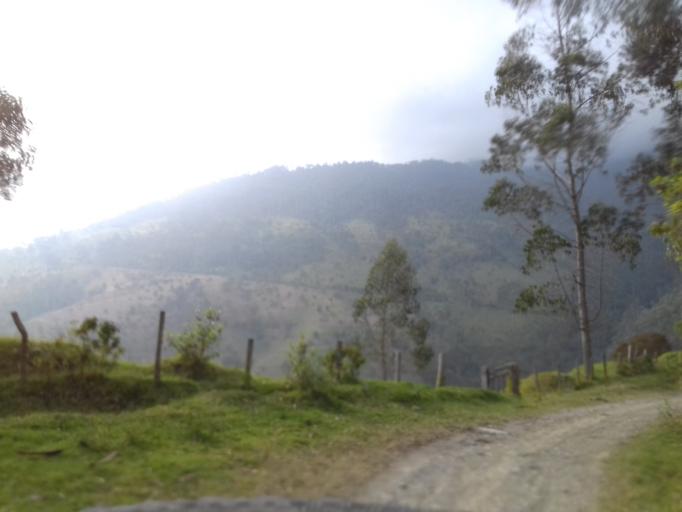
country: CO
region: Tolima
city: Cajamarca
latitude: 4.5326
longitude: -75.4364
